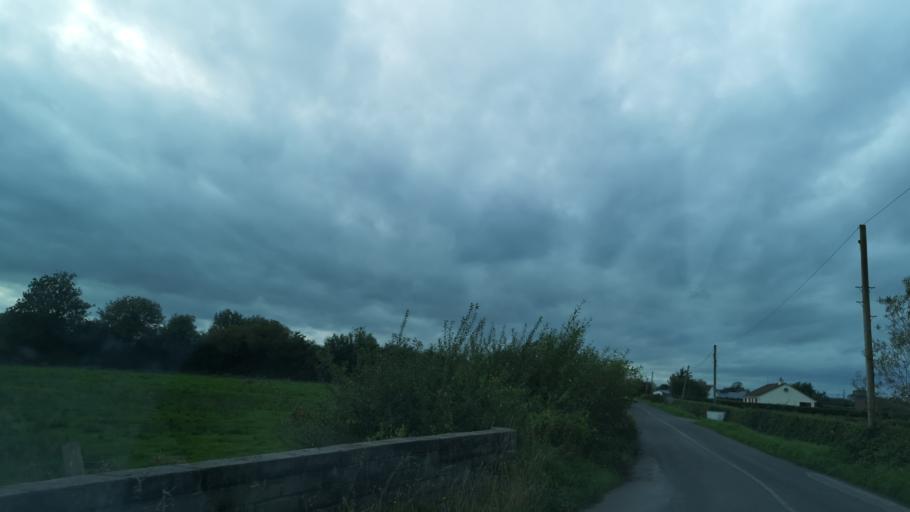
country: IE
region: Leinster
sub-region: Uibh Fhaili
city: Ferbane
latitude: 53.2180
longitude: -7.7935
